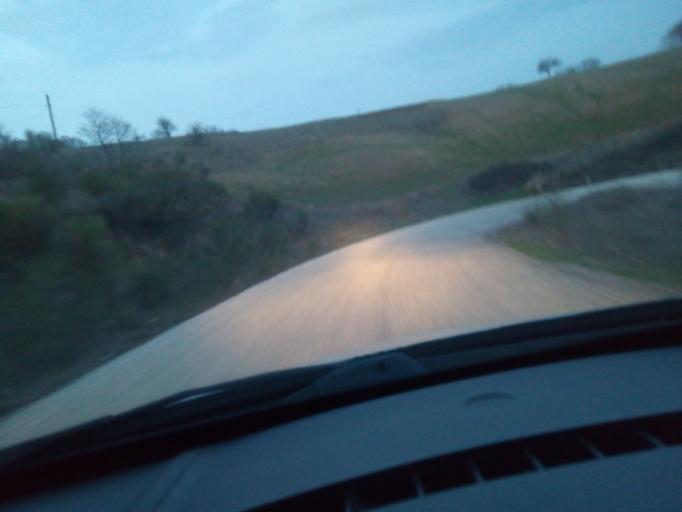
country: TR
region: Balikesir
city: Susurluk
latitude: 39.9099
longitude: 28.1073
